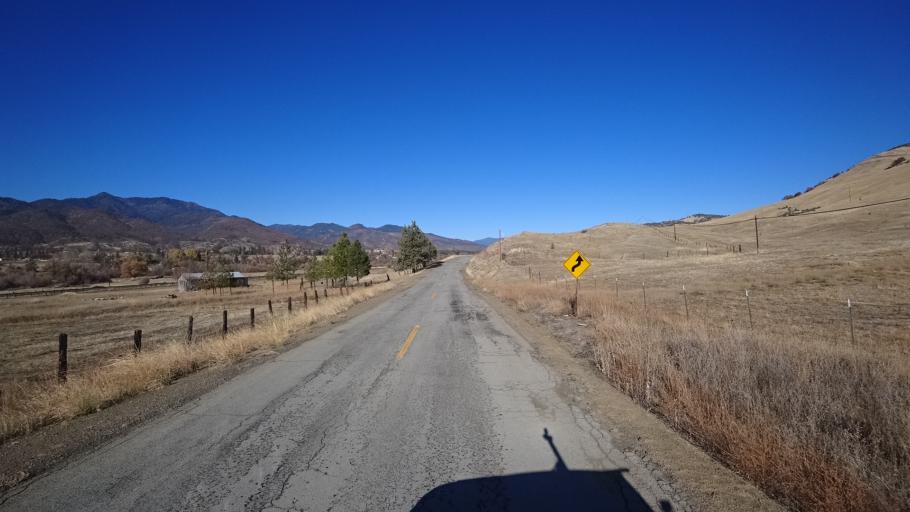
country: US
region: California
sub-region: Siskiyou County
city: Montague
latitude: 41.9019
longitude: -122.5453
